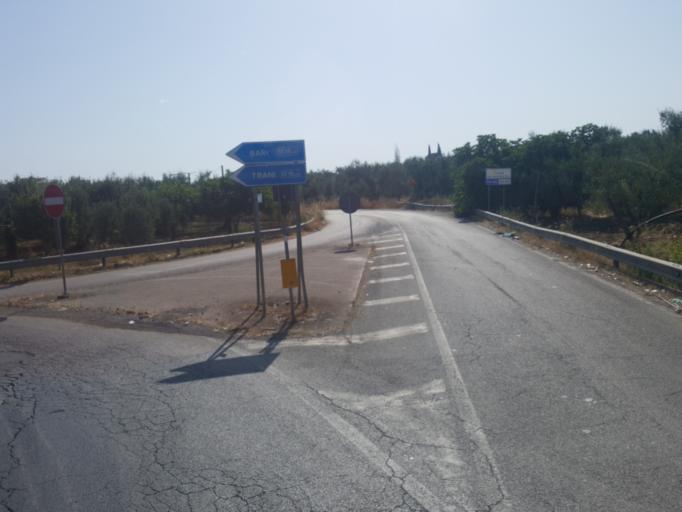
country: IT
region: Apulia
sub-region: Provincia di Barletta - Andria - Trani
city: Barletta
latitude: 41.3015
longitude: 16.3106
